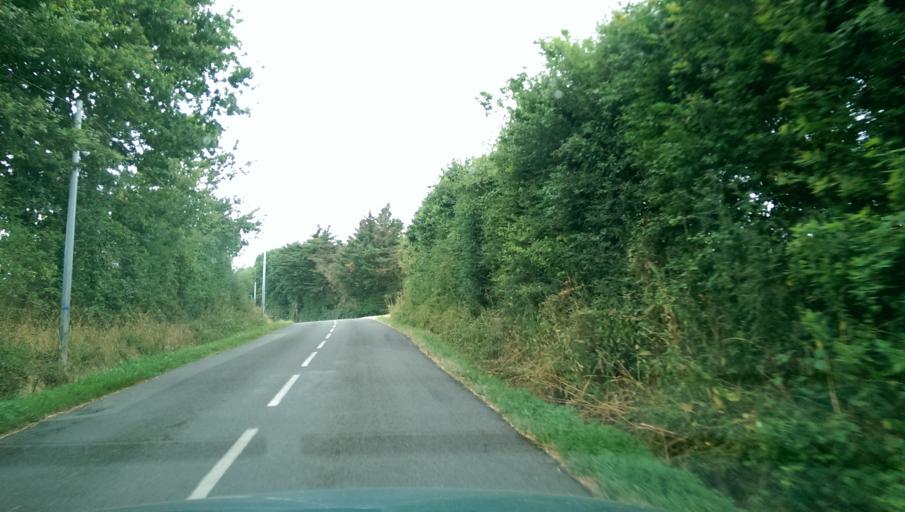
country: FR
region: Pays de la Loire
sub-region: Departement de la Loire-Atlantique
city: La Planche
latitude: 47.0037
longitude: -1.4065
